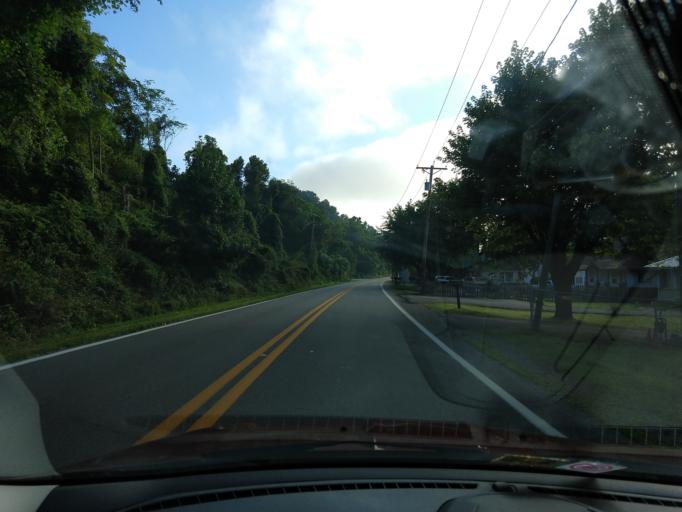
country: US
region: West Virginia
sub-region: Kanawha County
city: Charleston
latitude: 38.3852
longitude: -81.5935
